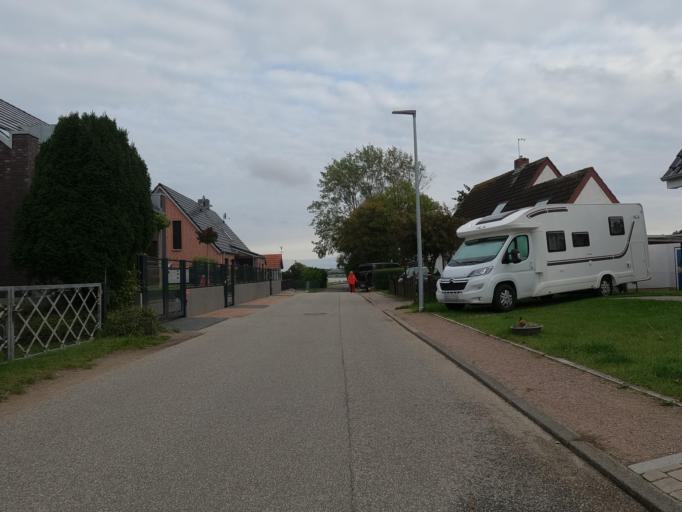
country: DE
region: Schleswig-Holstein
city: Heiligenhafen
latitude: 54.3701
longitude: 11.0097
